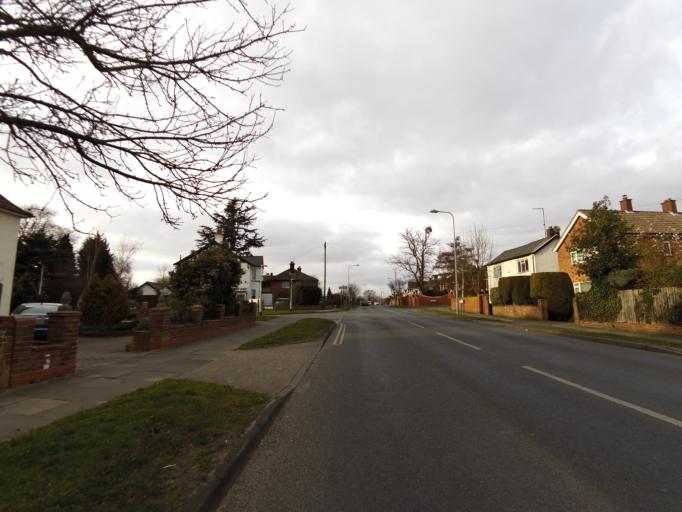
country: GB
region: England
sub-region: Suffolk
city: Ipswich
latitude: 52.0746
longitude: 1.1518
